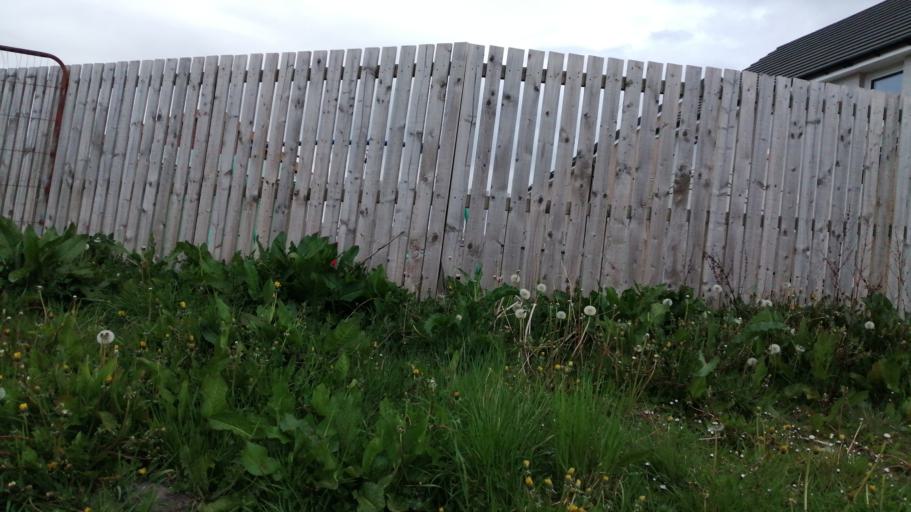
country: GB
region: Scotland
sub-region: Moray
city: Keith
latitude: 57.5361
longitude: -2.9424
